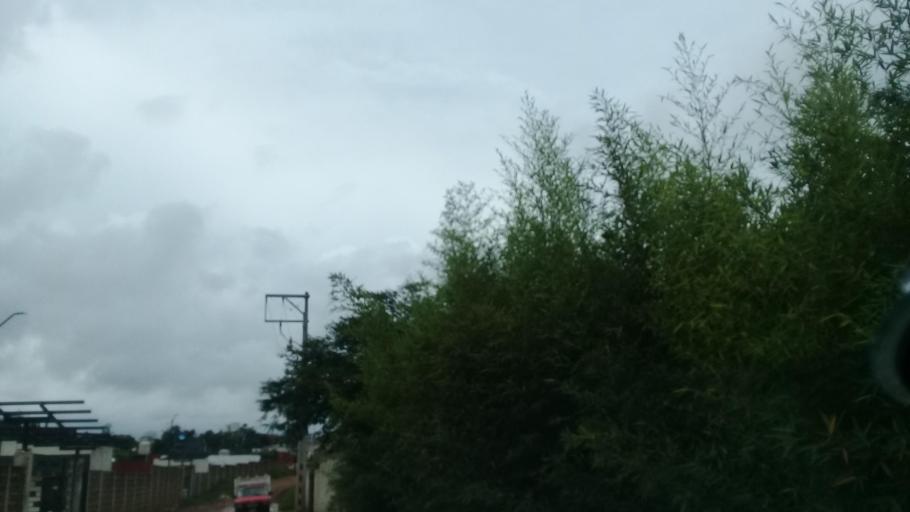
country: MX
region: Veracruz
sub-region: Emiliano Zapata
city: Las Trancas
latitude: 19.4976
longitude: -96.8678
